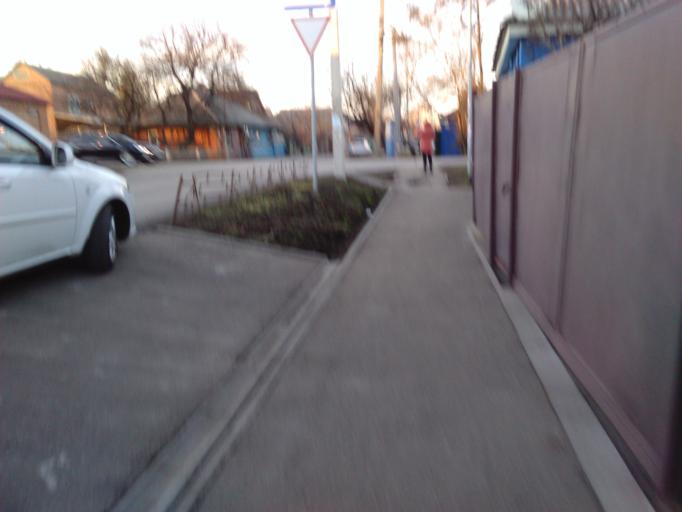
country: RU
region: Rostov
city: Bataysk
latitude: 47.1491
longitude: 39.7414
